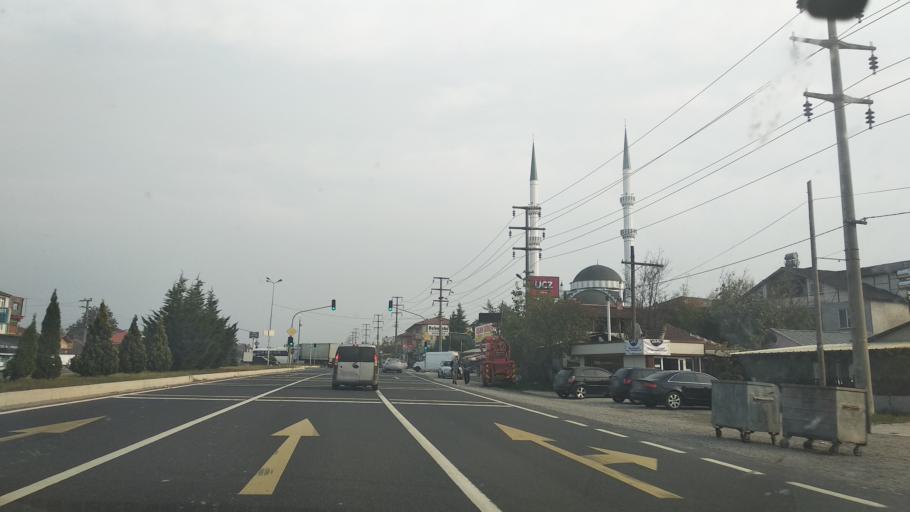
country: TR
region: Duzce
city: Duzce
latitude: 40.8037
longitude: 31.2361
